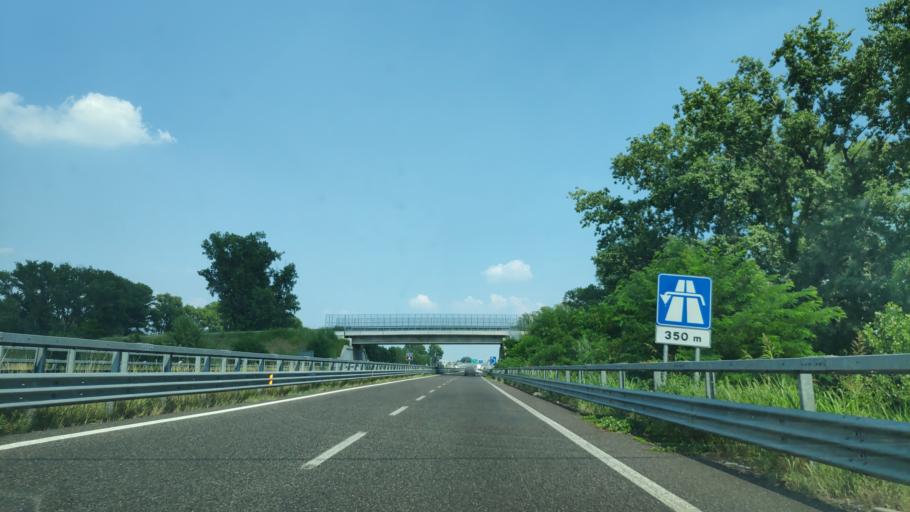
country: IT
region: Lombardy
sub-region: Citta metropolitana di Milano
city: Lucino-Rodano
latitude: 45.4839
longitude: 9.3665
